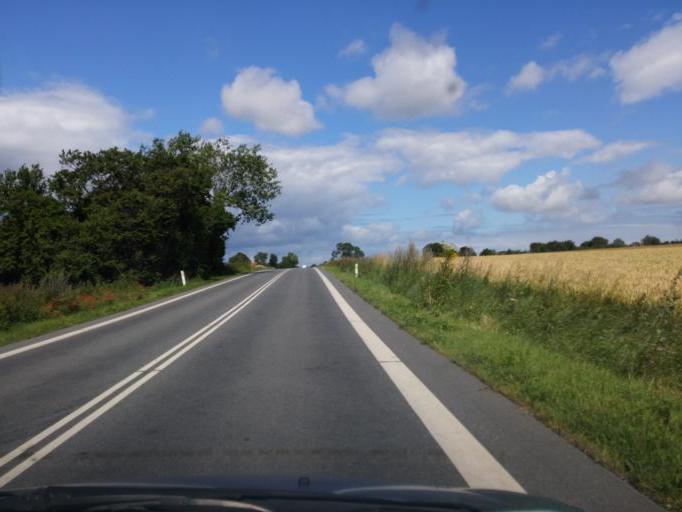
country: DK
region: South Denmark
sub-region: Kerteminde Kommune
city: Kerteminde
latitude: 55.4680
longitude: 10.6765
